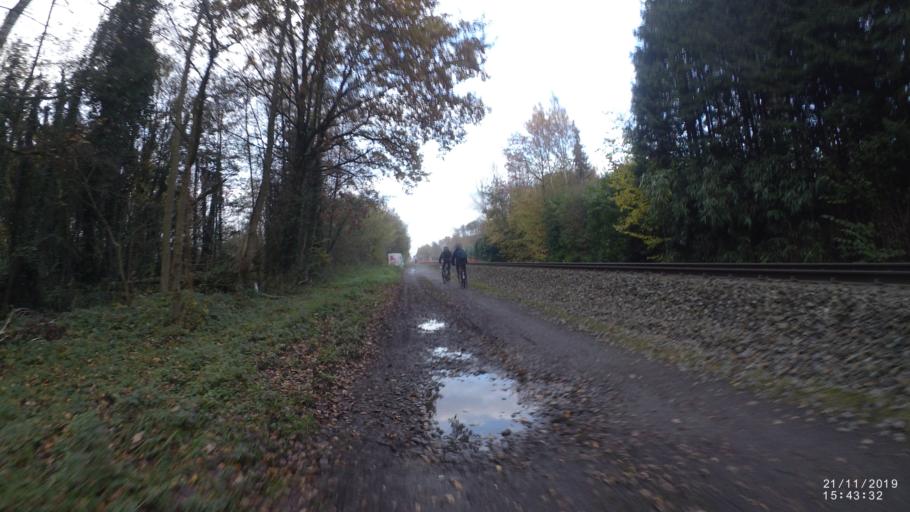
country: BE
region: Flanders
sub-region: Provincie Limburg
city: Zonhoven
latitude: 50.9660
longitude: 5.3433
